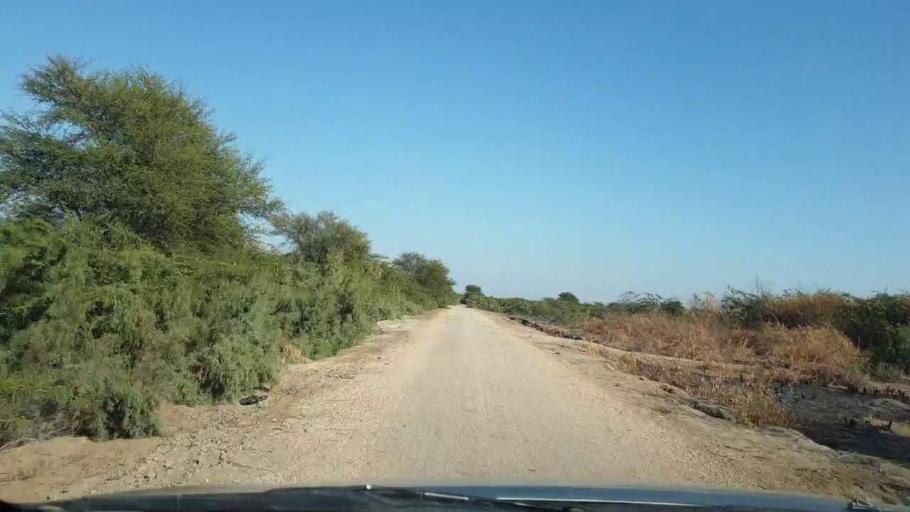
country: PK
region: Sindh
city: Jhol
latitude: 25.8515
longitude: 68.9560
